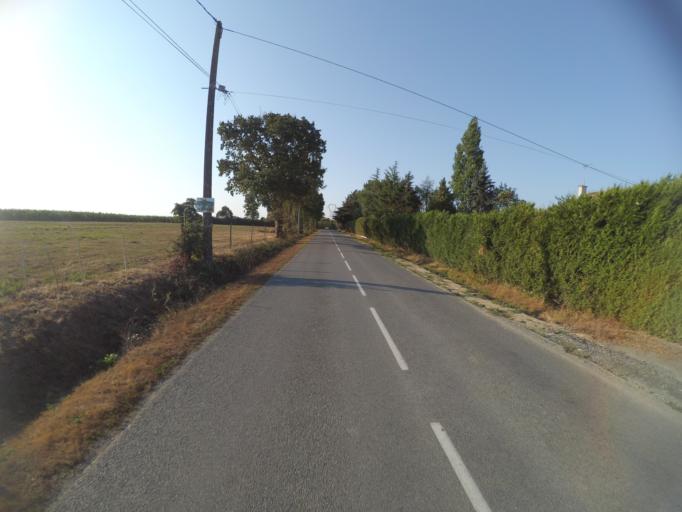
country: FR
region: Pays de la Loire
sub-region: Departement de la Loire-Atlantique
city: La Planche
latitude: 47.0236
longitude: -1.4211
